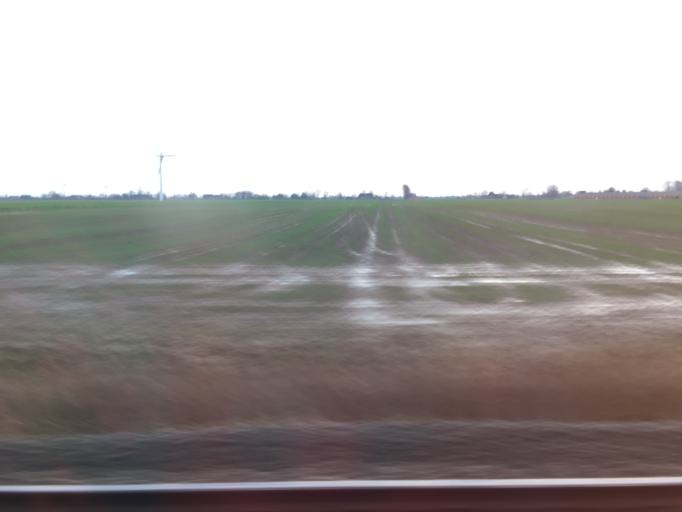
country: DE
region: Schleswig-Holstein
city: Krempdorf
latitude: 53.8183
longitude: 9.4605
